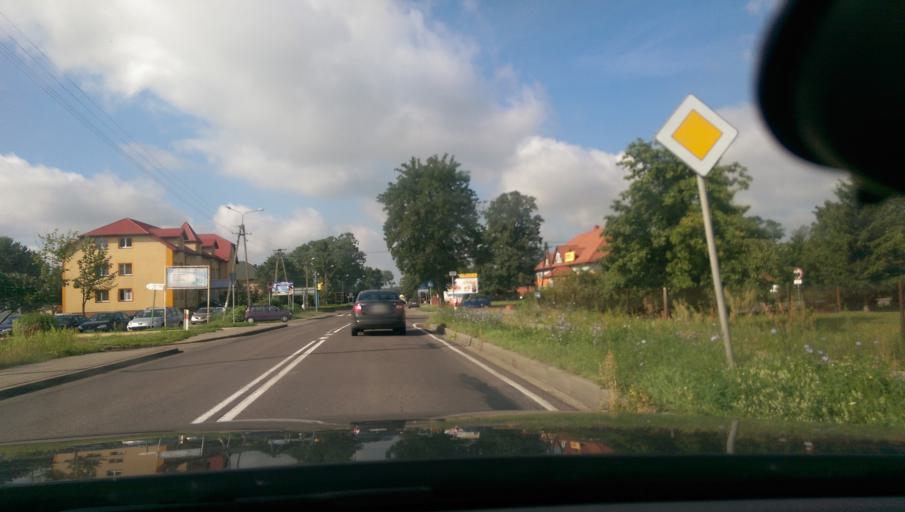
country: PL
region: Masovian Voivodeship
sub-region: Powiat ciechanowski
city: Ojrzen
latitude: 52.7695
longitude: 20.5453
